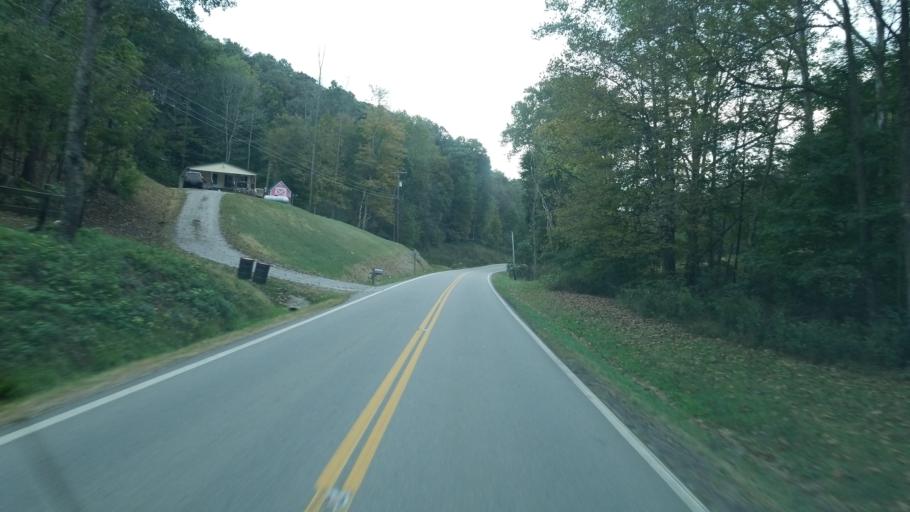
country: US
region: Ohio
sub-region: Meigs County
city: Pomeroy
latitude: 39.1034
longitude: -82.0981
